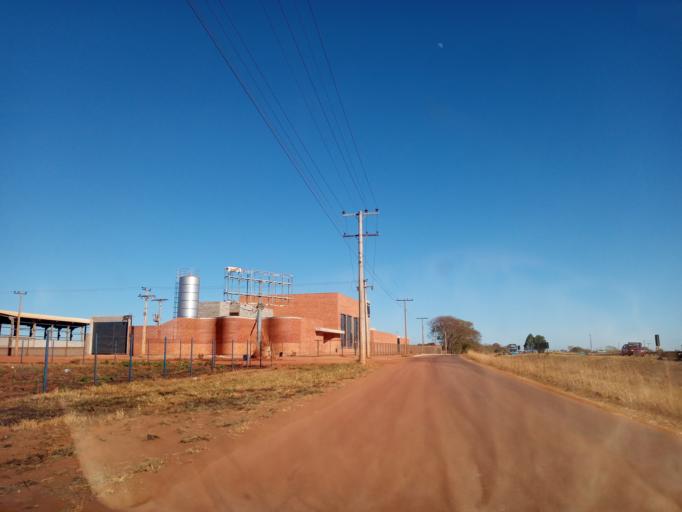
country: BR
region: Goias
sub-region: Abadiania
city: Abadiania
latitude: -16.1208
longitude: -48.4277
